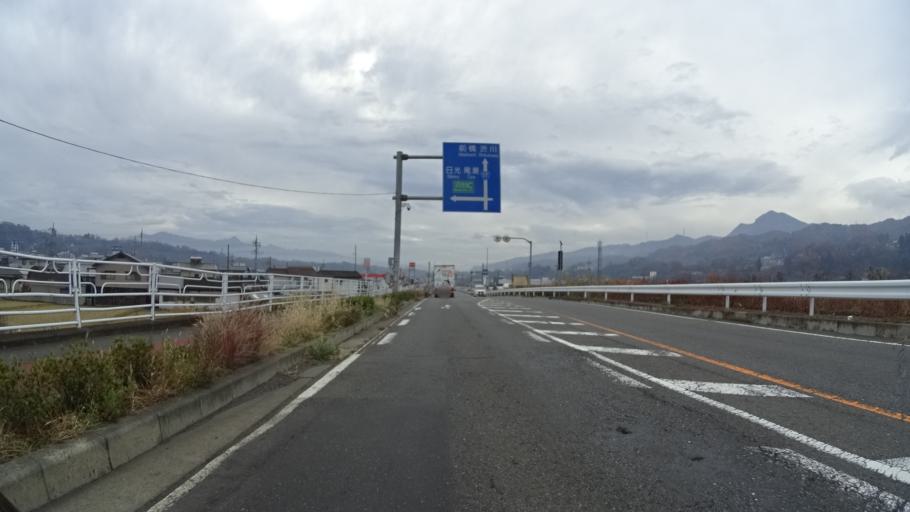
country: JP
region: Gunma
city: Numata
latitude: 36.6457
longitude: 139.0282
